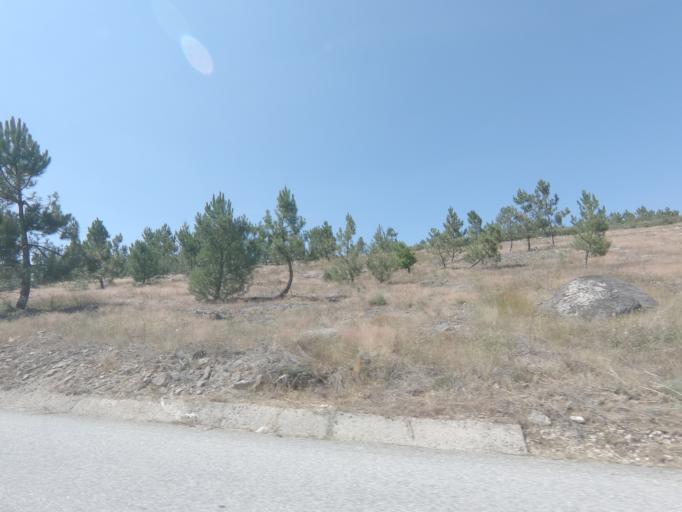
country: PT
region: Viseu
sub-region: Tarouca
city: Tarouca
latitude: 40.9827
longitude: -7.7917
